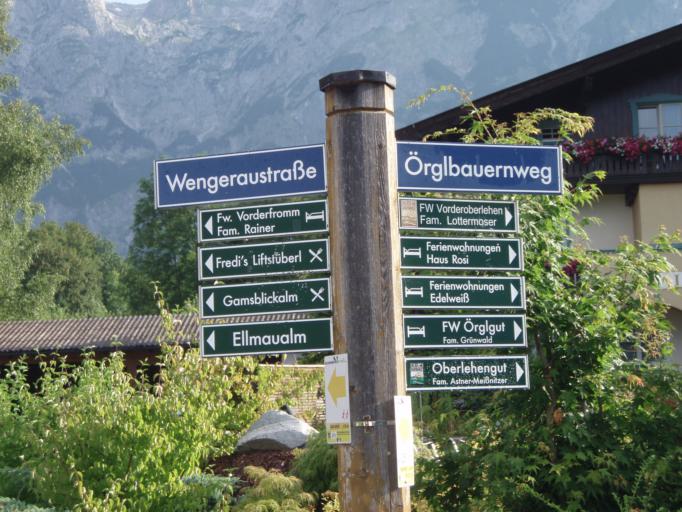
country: AT
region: Salzburg
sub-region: Politischer Bezirk Sankt Johann im Pongau
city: Werfenweng
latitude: 47.4679
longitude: 13.2635
